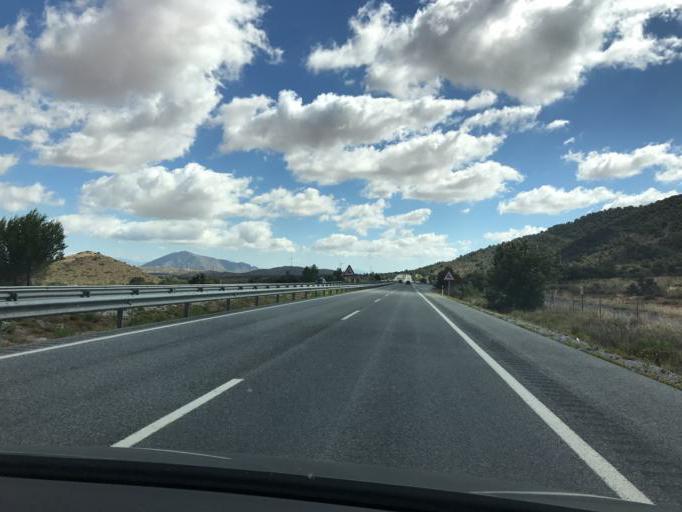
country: ES
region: Andalusia
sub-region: Provincia de Granada
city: Freila
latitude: 37.4613
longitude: -2.8709
